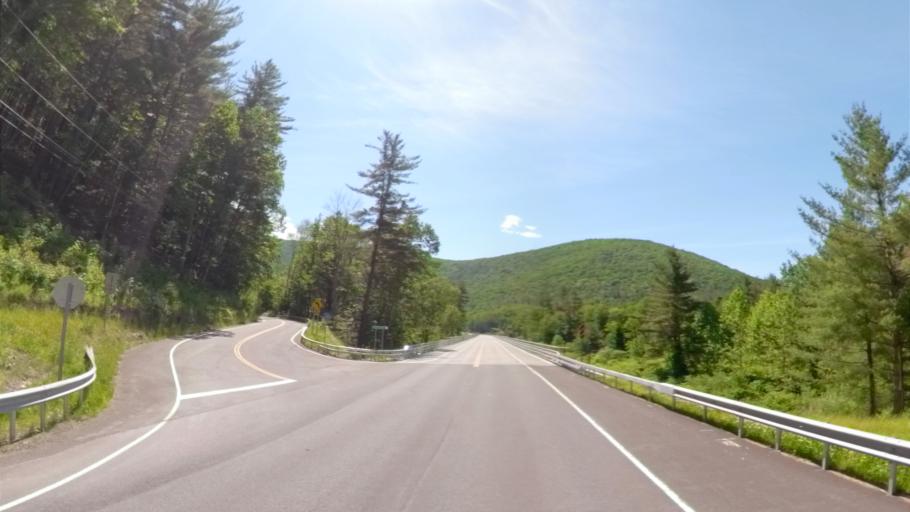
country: US
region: New York
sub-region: Ulster County
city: Shokan
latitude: 42.1061
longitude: -74.4488
